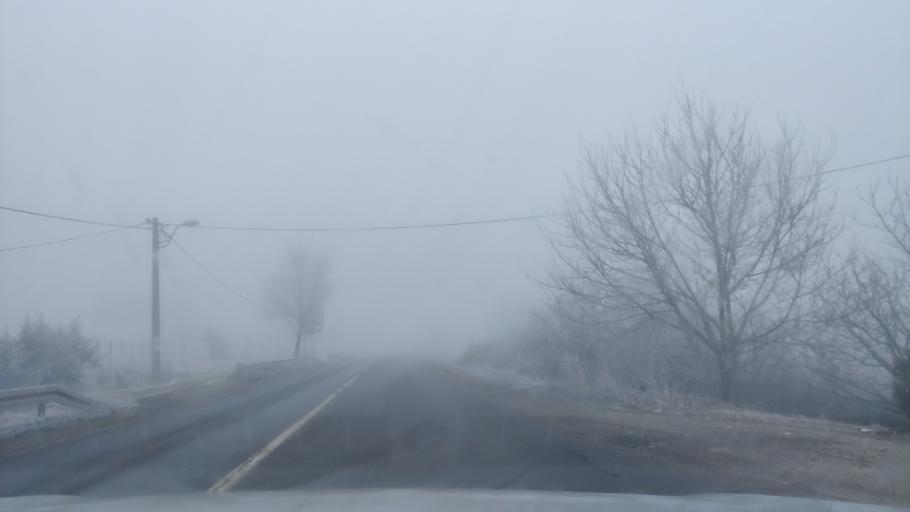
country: RS
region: Central Serbia
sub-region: Belgrade
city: Stari Grad
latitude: 44.8924
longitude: 20.4575
